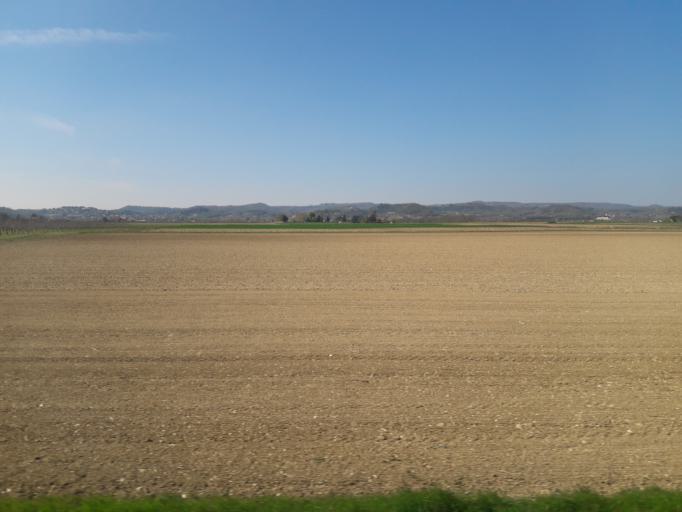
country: FR
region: Rhone-Alpes
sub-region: Departement de la Drome
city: Saint-Paul-les-Romans
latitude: 45.0647
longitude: 5.1141
